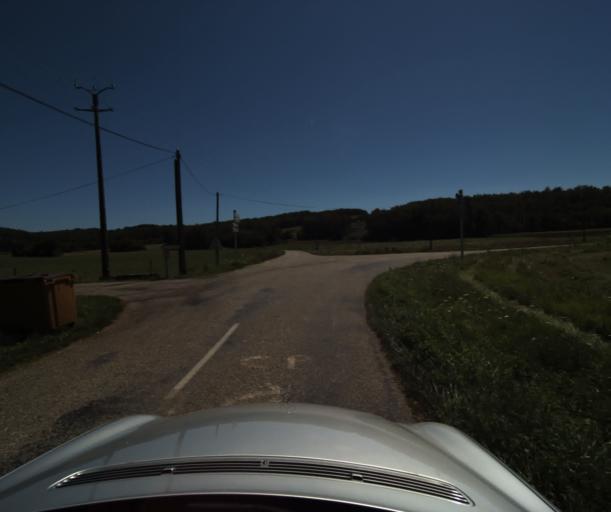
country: FR
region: Midi-Pyrenees
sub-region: Departement de l'Ariege
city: Belesta
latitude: 42.9813
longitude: 1.9167
